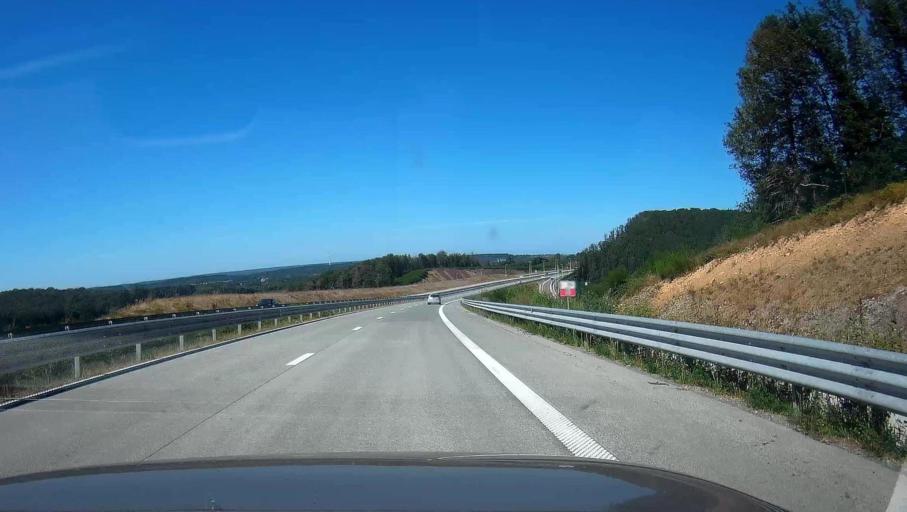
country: BE
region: Wallonia
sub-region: Province de Namur
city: Couvin
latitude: 50.0333
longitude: 4.5081
